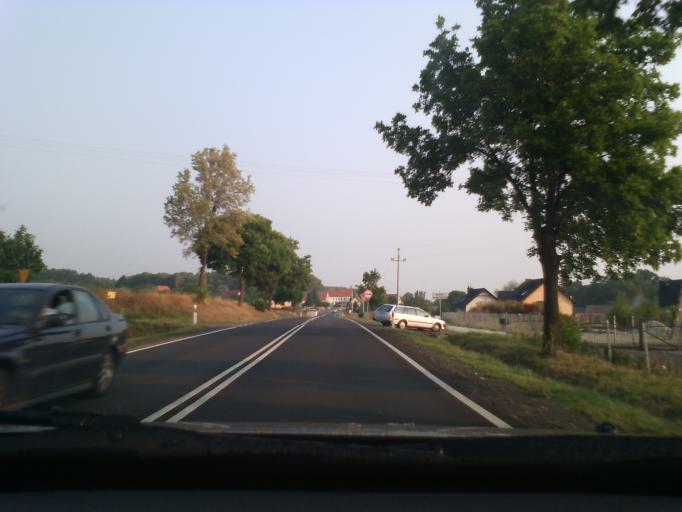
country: PL
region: Lower Silesian Voivodeship
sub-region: Powiat swidnicki
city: Swiebodzice
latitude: 50.8923
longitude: 16.2625
